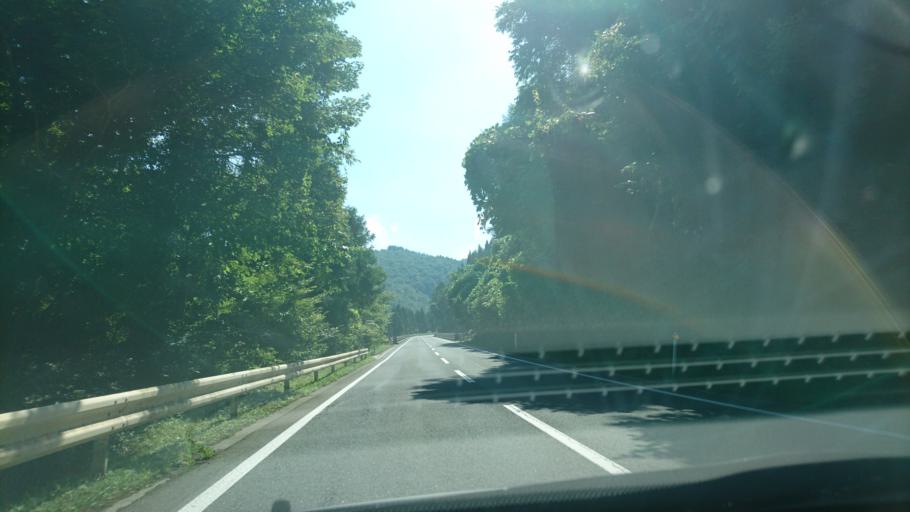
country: JP
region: Iwate
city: Ofunato
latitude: 39.0110
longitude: 141.4847
